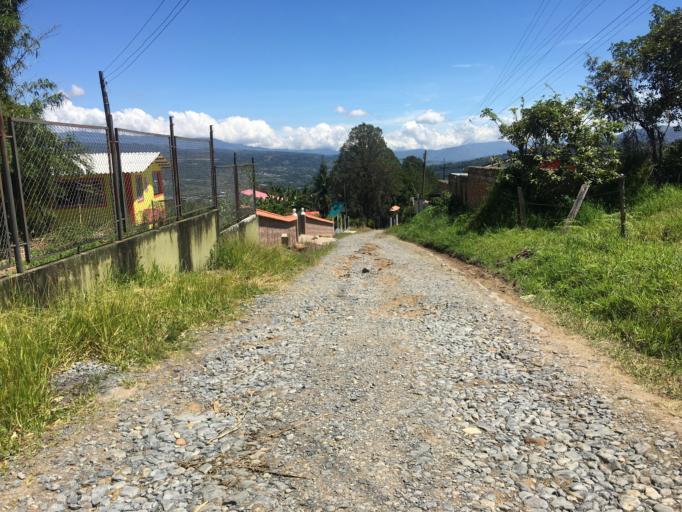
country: CO
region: Santander
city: Barbosa
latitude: 5.9111
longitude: -73.5984
